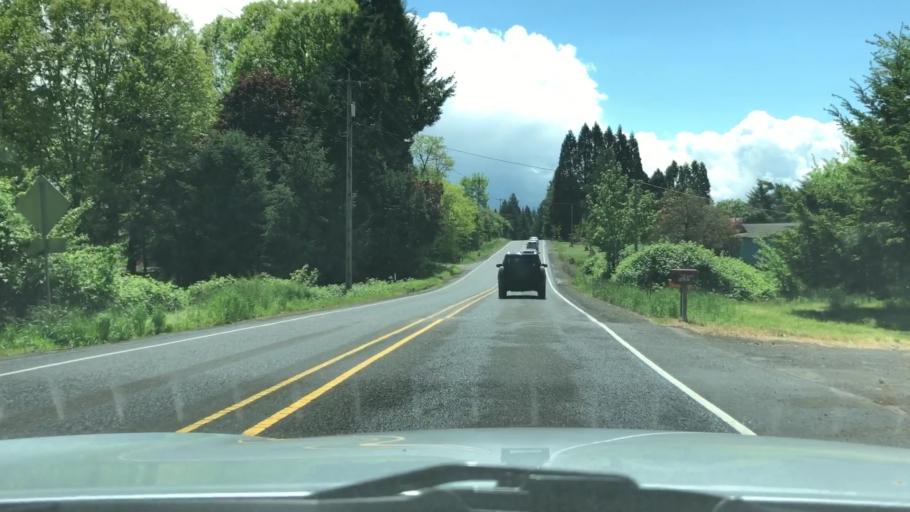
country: US
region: Oregon
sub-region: Clackamas County
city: Beavercreek
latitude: 45.3077
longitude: -122.5461
